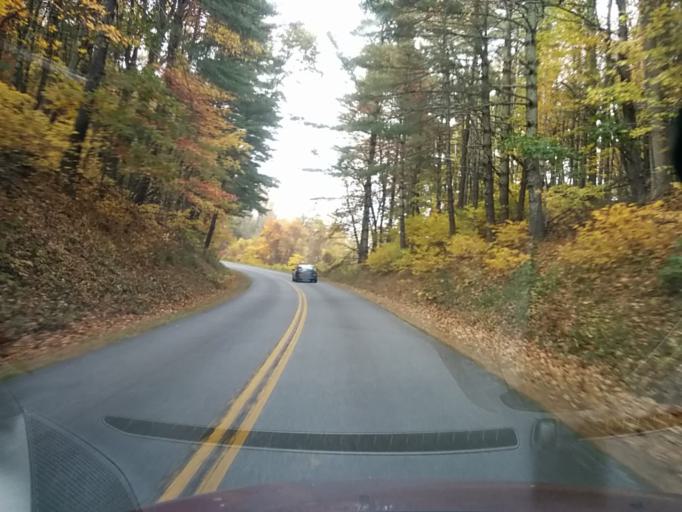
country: US
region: Virginia
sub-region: City of Buena Vista
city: Buena Vista
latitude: 37.8016
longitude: -79.2175
